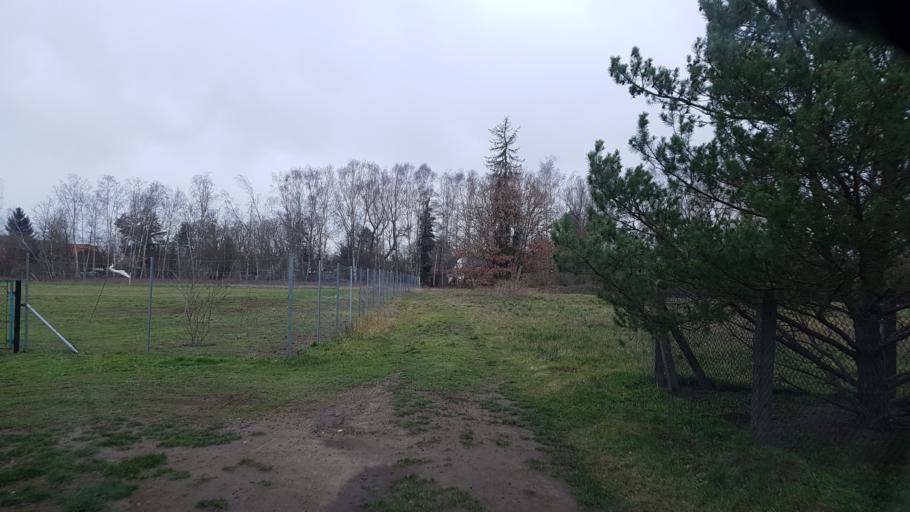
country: DE
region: Brandenburg
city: Herzberg
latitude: 51.6983
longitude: 13.2334
